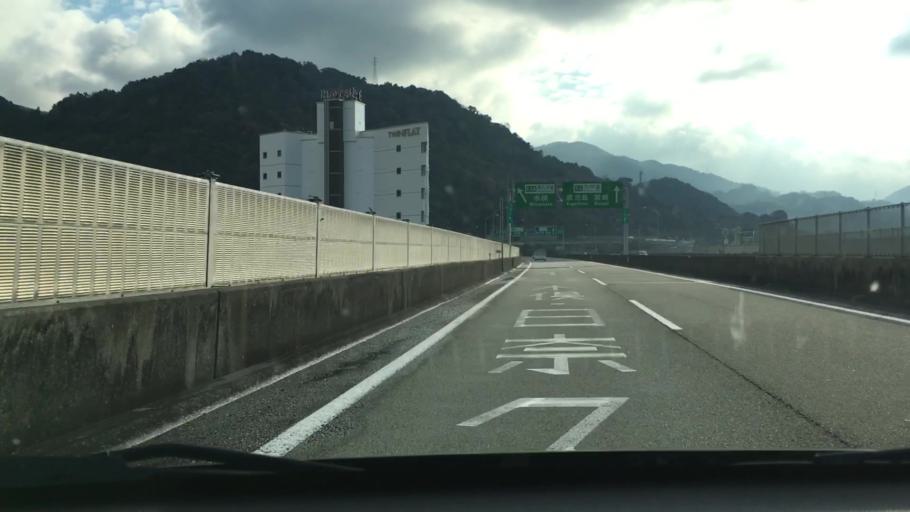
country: JP
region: Kumamoto
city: Yatsushiro
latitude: 32.5076
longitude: 130.6465
